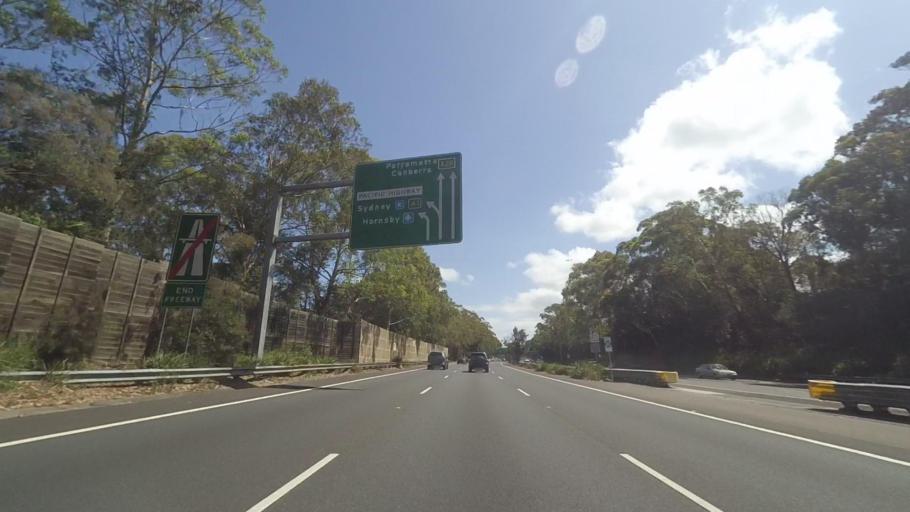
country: AU
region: New South Wales
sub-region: Ku-ring-gai
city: North Wahroonga
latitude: -33.7122
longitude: 151.1153
